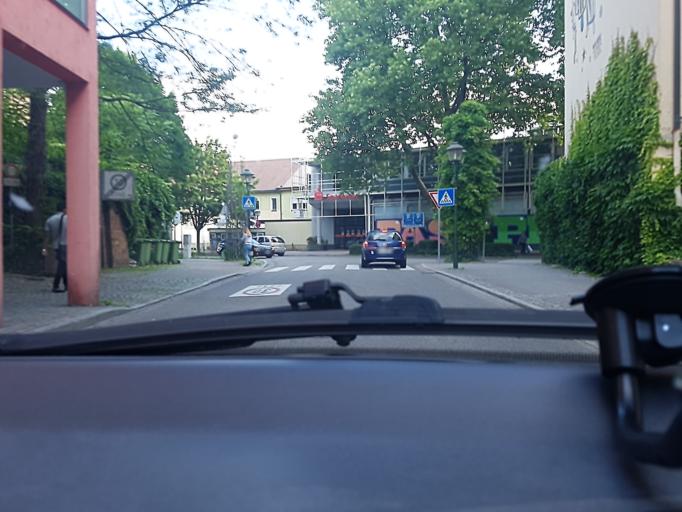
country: DE
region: Baden-Wuerttemberg
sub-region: Freiburg Region
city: Offenburg
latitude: 48.4717
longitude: 7.9443
